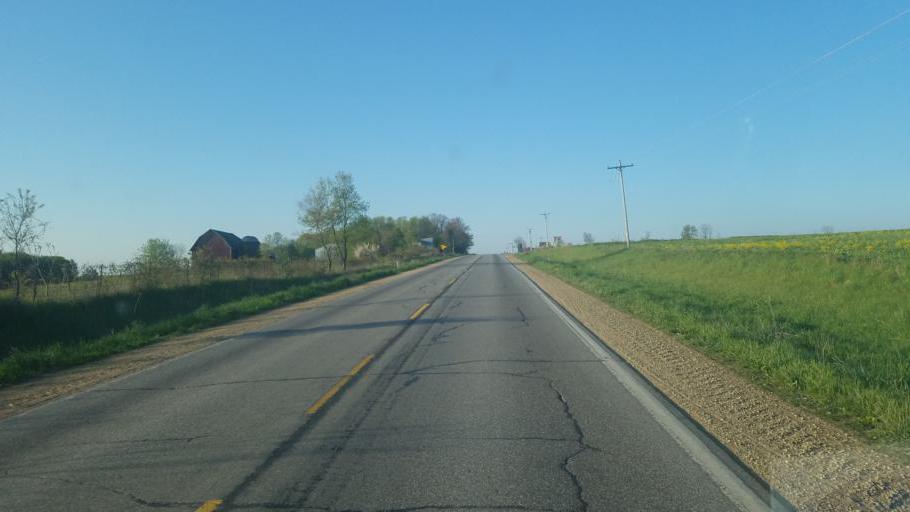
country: US
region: Wisconsin
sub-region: Vernon County
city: Hillsboro
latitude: 43.6270
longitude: -90.4525
